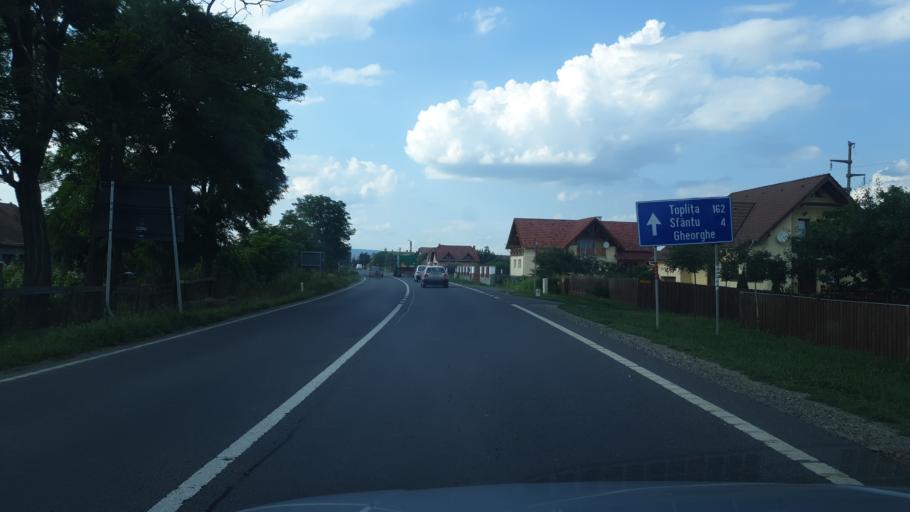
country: RO
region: Covasna
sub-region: Municipiul Sfantu Gheorghe
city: Sfantu-Gheorghe
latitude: 45.8331
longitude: 25.8045
